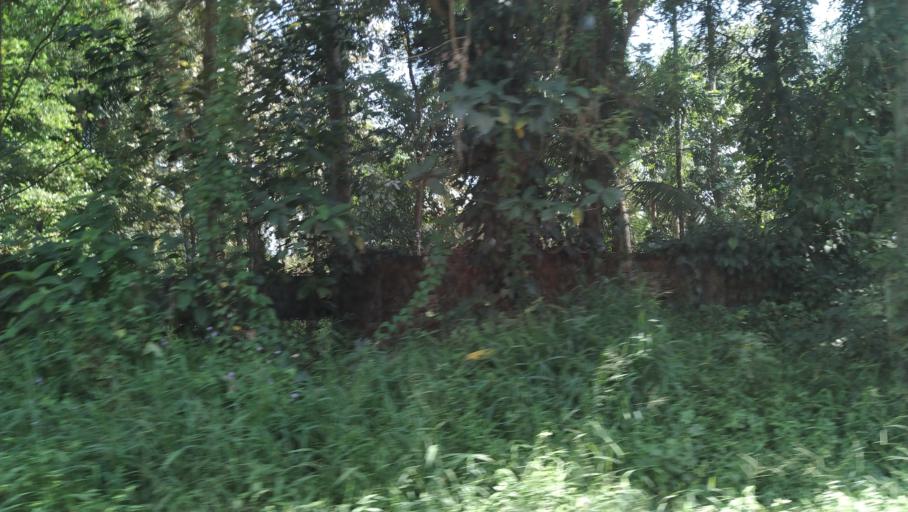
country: IN
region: Kerala
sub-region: Ernakulam
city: Aluva
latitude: 10.1280
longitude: 76.3512
